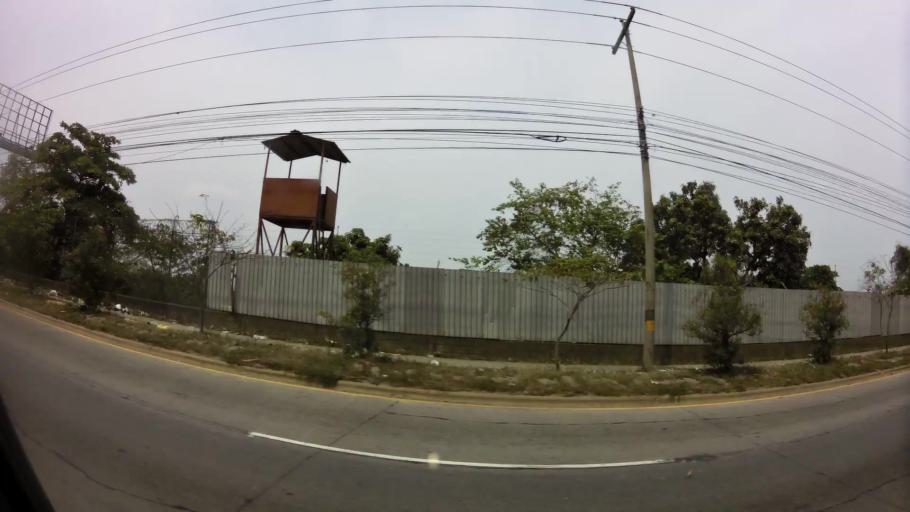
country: HN
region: Cortes
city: San Pedro Sula
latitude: 15.4594
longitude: -88.0281
